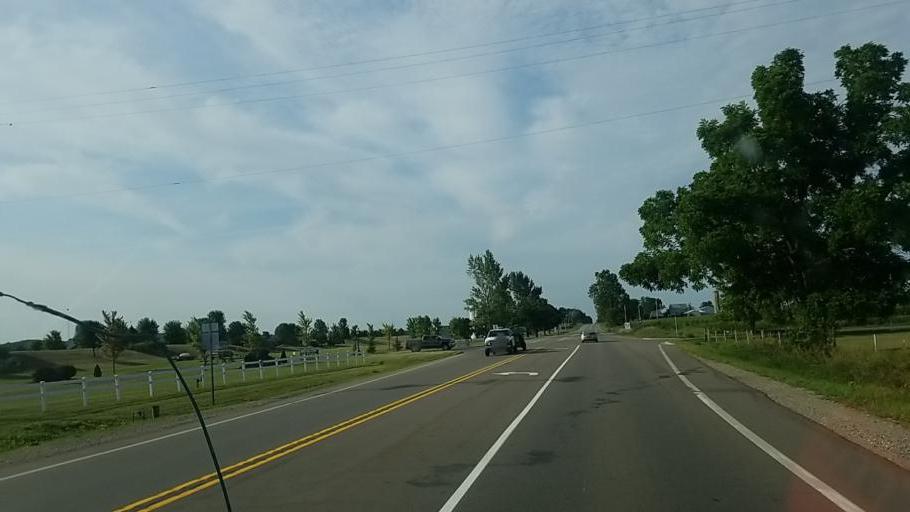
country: US
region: Michigan
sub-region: Ionia County
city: Ionia
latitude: 42.9158
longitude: -85.0748
